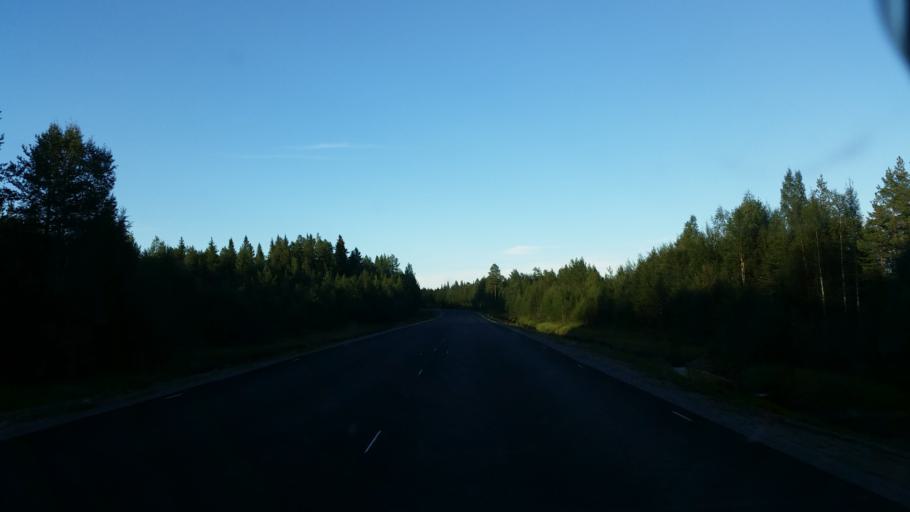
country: SE
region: Vaesterbotten
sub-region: Dorotea Kommun
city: Dorotea
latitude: 64.2885
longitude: 16.5180
